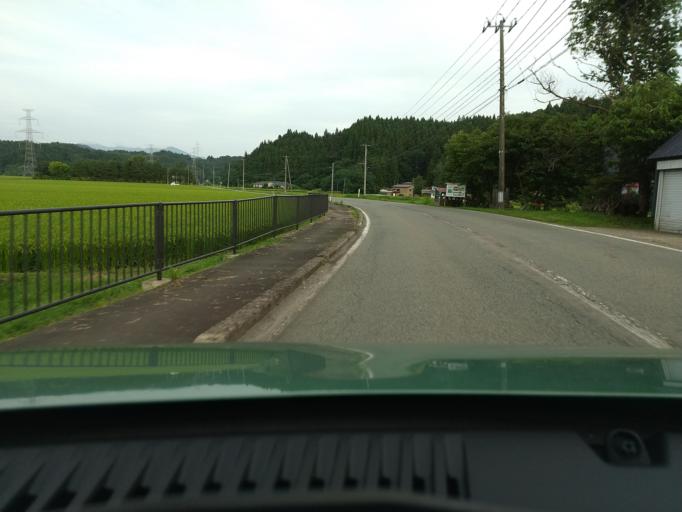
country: JP
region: Akita
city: Akita Shi
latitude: 39.7897
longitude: 140.1136
